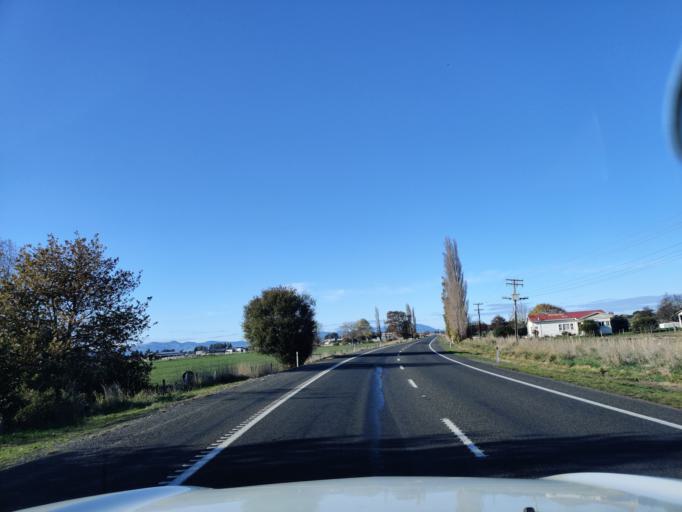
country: NZ
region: Waikato
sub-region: Hauraki District
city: Ngatea
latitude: -37.2851
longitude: 175.5459
